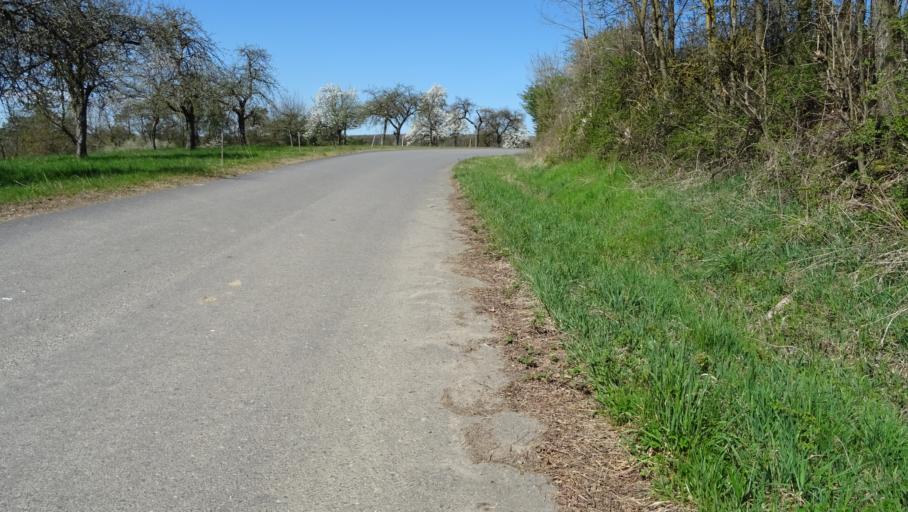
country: DE
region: Baden-Wuerttemberg
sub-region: Karlsruhe Region
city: Billigheim
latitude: 49.4005
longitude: 9.2357
